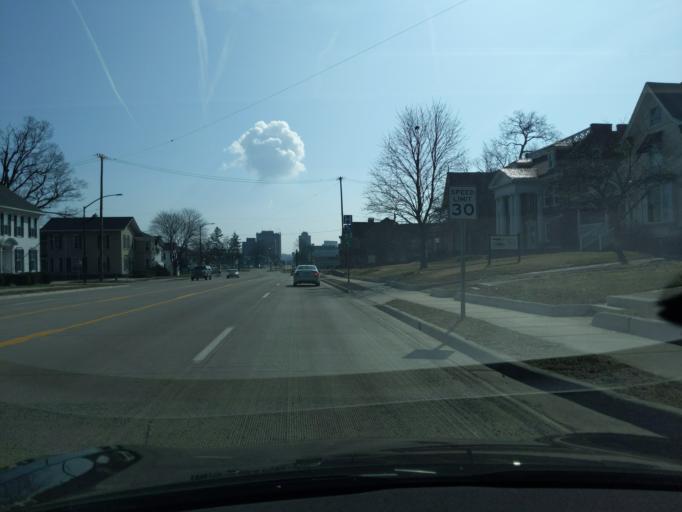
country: US
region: Michigan
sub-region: Jackson County
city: Jackson
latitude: 42.2474
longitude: -84.4184
